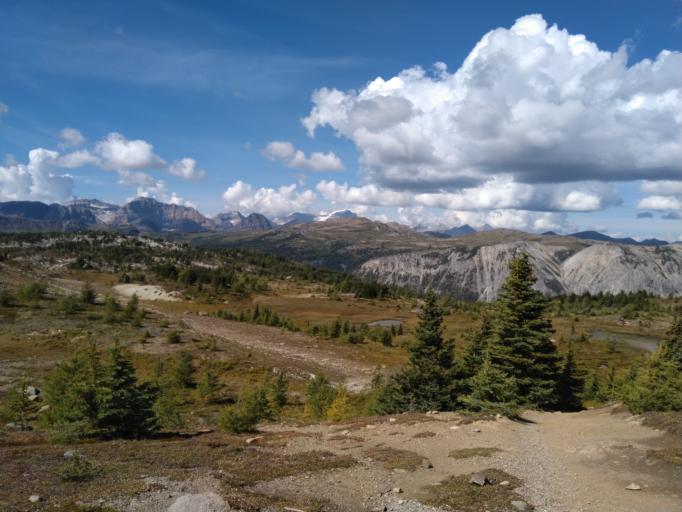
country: CA
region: Alberta
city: Banff
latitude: 51.0854
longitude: -115.7974
